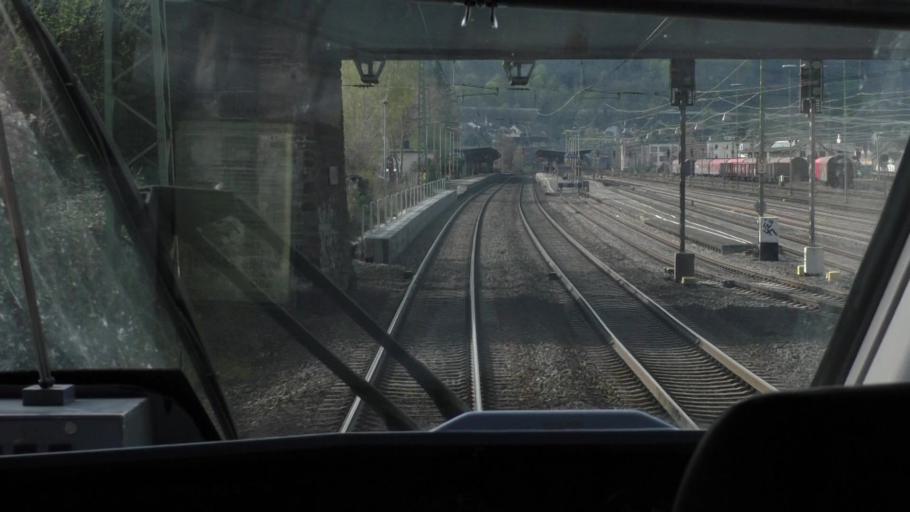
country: DE
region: Rheinland-Pfalz
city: Andernach
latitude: 50.4328
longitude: 7.4104
